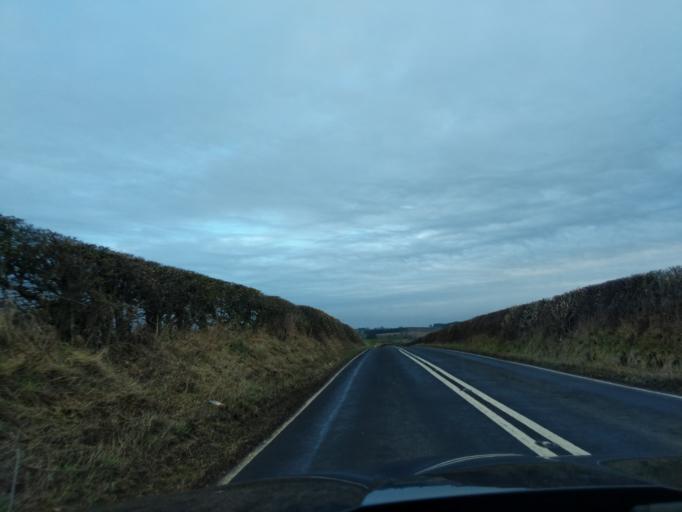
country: GB
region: England
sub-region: Northumberland
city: Rothley
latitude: 55.1169
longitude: -1.9034
